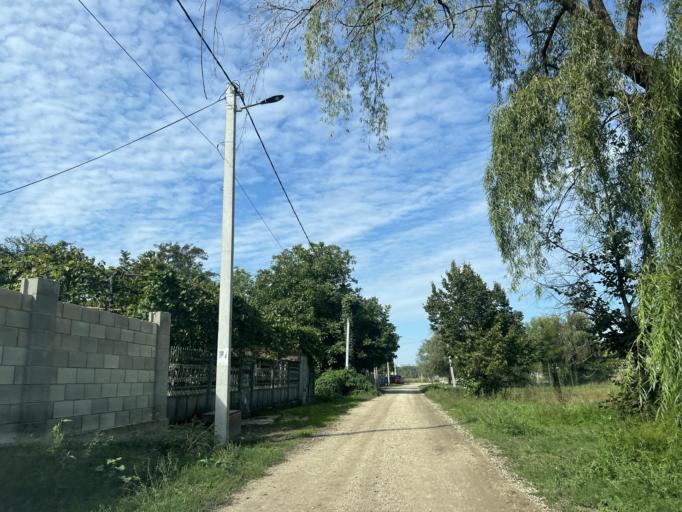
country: MD
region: Ungheni
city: Ungheni
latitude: 47.1956
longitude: 27.8127
